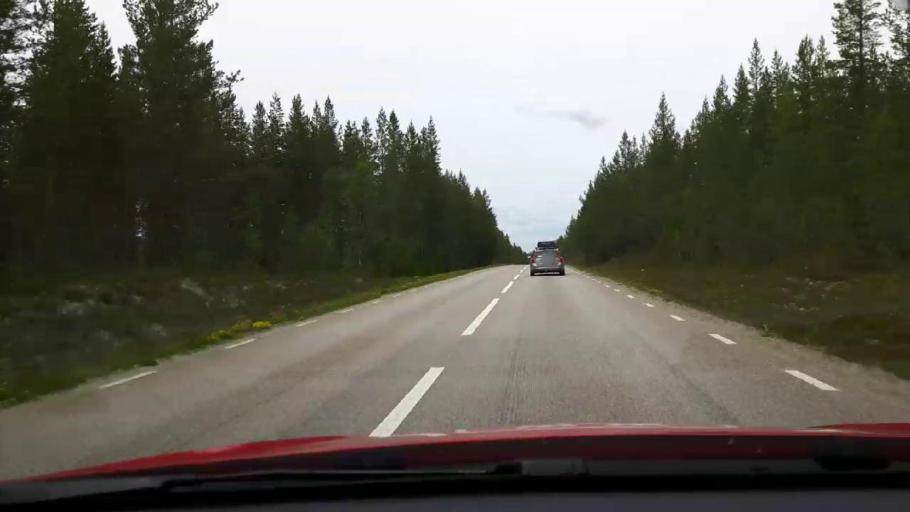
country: SE
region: Jaemtland
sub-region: Harjedalens Kommun
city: Sveg
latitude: 62.2294
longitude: 13.8580
